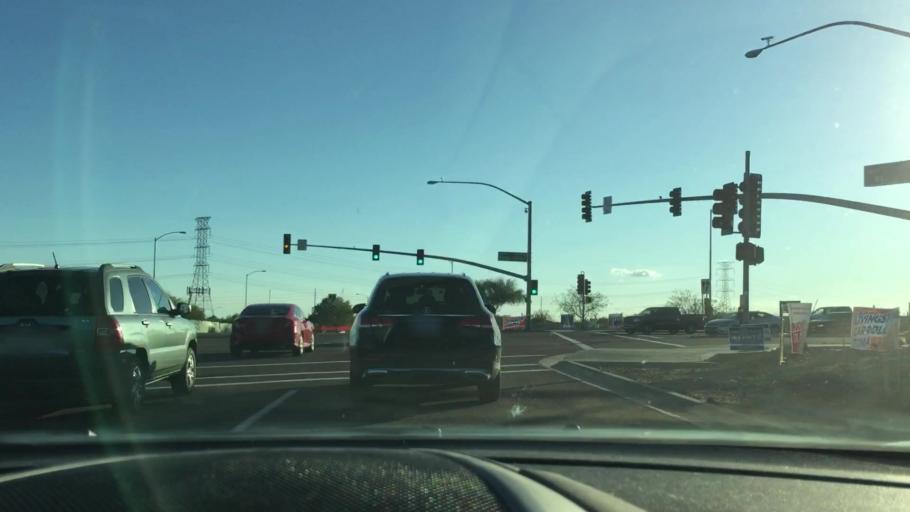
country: US
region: Arizona
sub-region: Maricopa County
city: Sun City West
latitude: 33.7096
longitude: -112.2358
